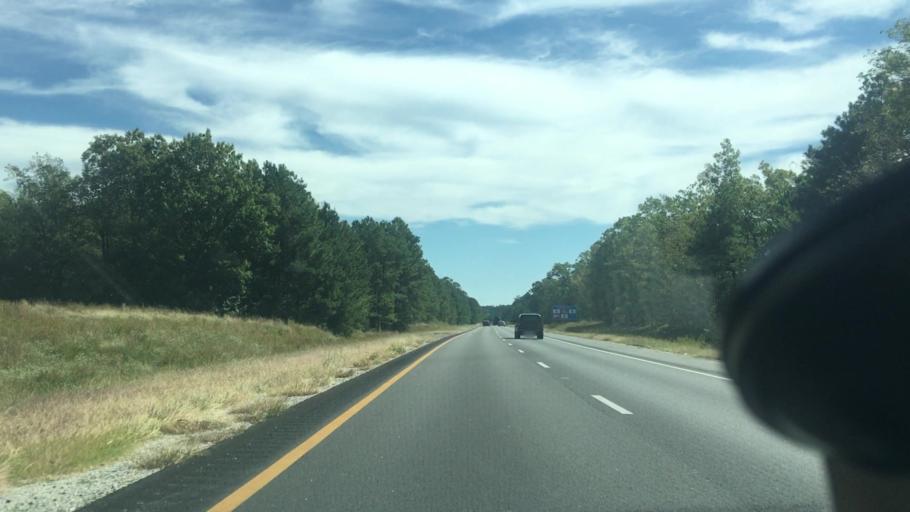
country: US
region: Virginia
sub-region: Chesterfield County
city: Chesterfield
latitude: 37.4020
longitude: -77.5342
